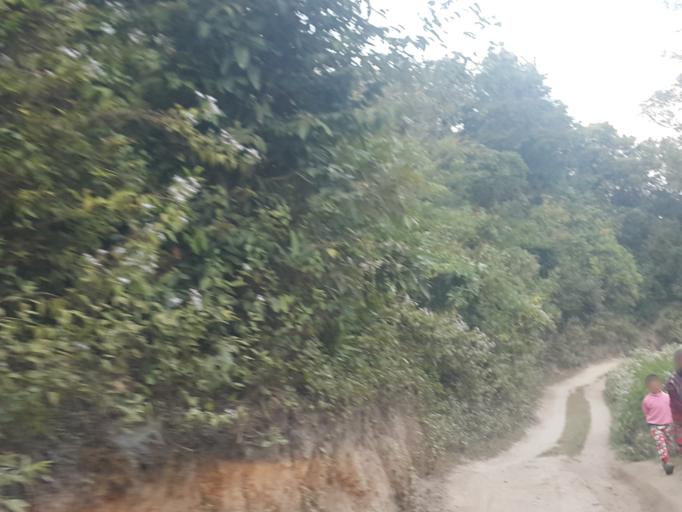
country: TH
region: Chiang Mai
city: Om Koi
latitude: 17.7778
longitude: 98.2996
